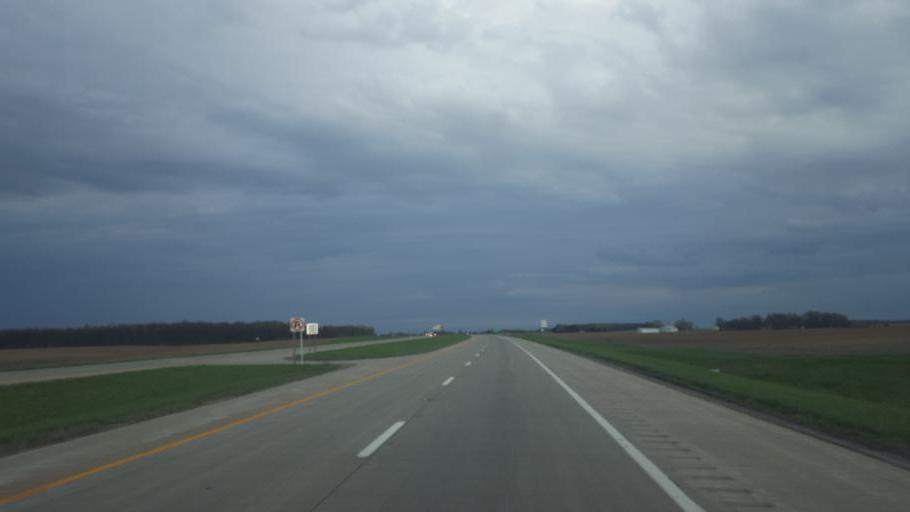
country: US
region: Ohio
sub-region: Wyandot County
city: Upper Sandusky
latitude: 40.8080
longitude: -83.2193
